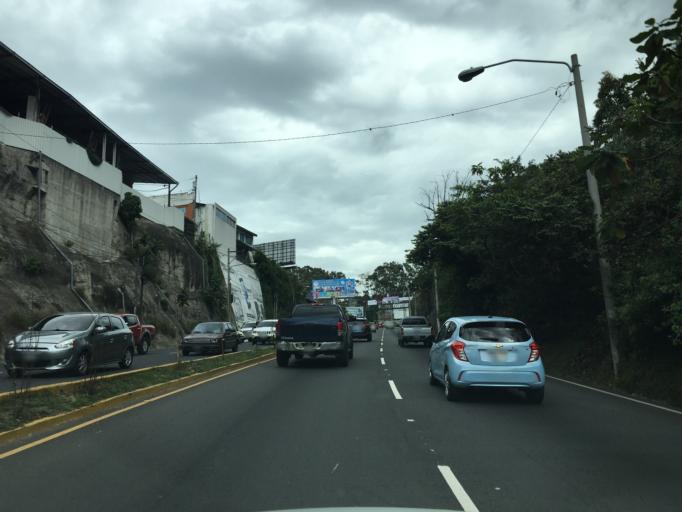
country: GT
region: Guatemala
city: Mixco
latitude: 14.5953
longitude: -90.5696
